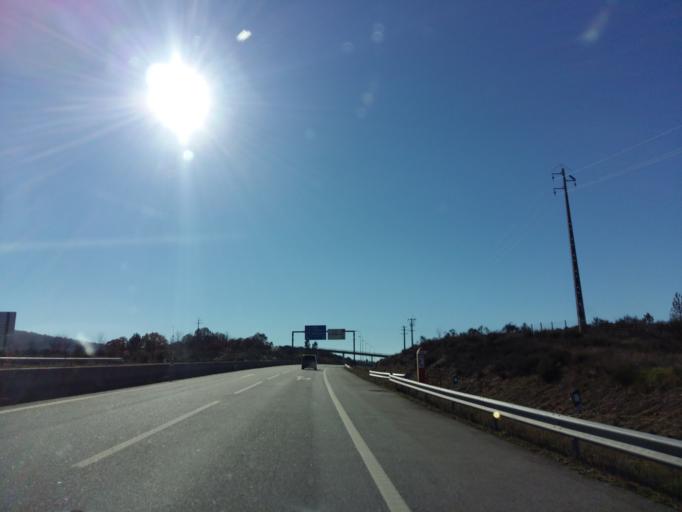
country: PT
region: Castelo Branco
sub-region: Covilha
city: Covilha
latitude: 40.2342
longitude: -7.4840
